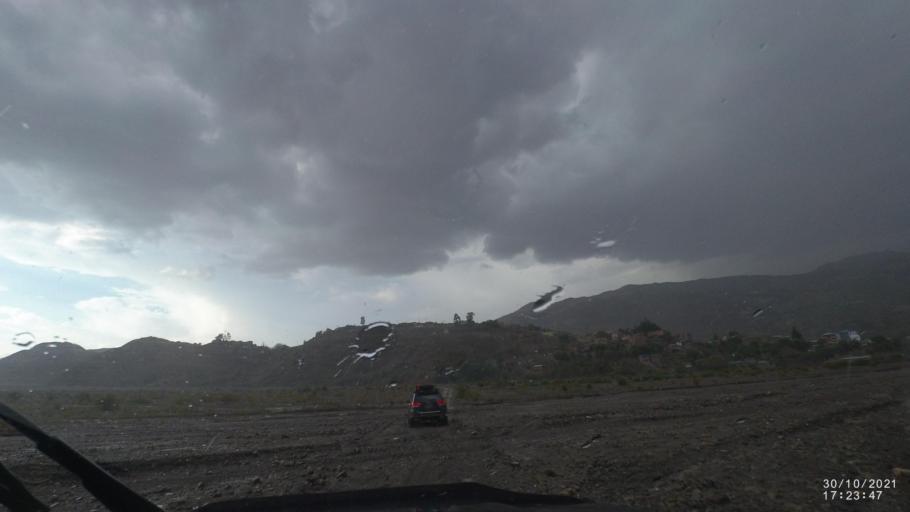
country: BO
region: Cochabamba
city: Colchani
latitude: -17.5203
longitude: -66.6223
